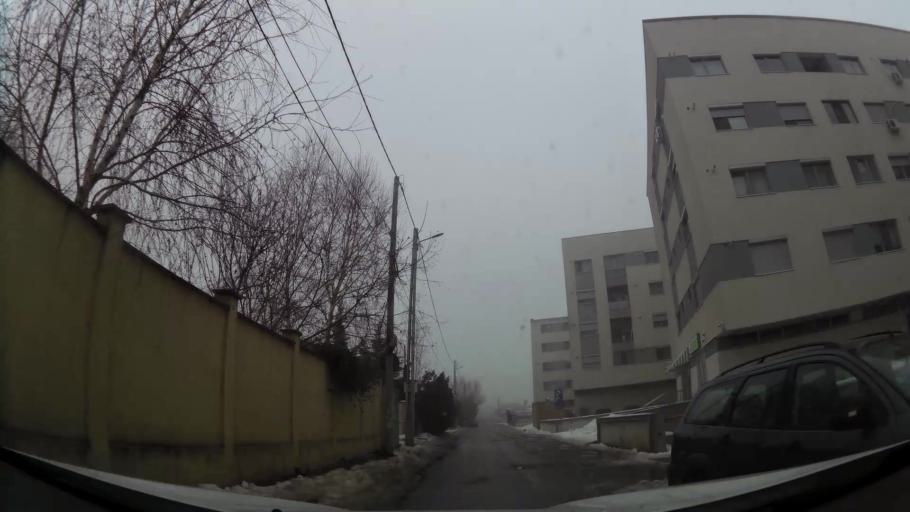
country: RO
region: Ilfov
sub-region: Comuna Chiajna
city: Chiajna
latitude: 44.4516
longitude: 25.9875
